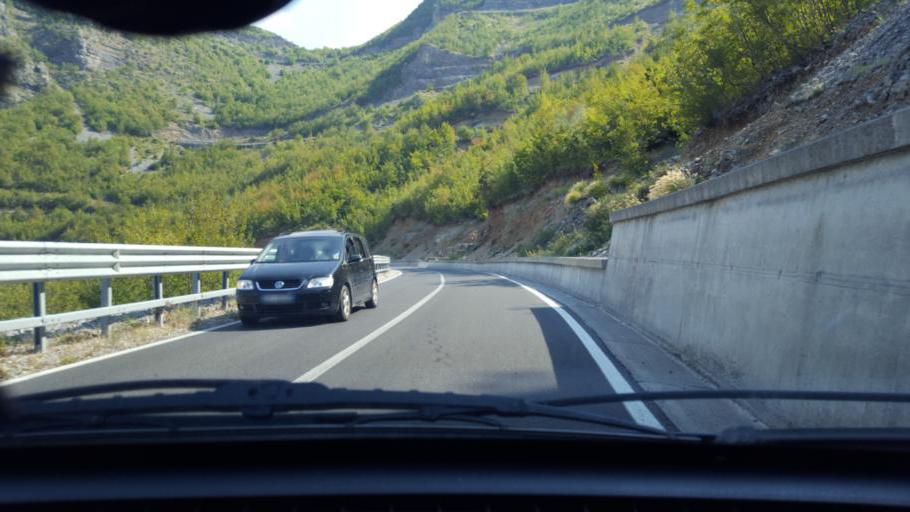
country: AL
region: Shkoder
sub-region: Rrethi i Malesia e Madhe
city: Kastrat
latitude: 42.4161
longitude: 19.4973
